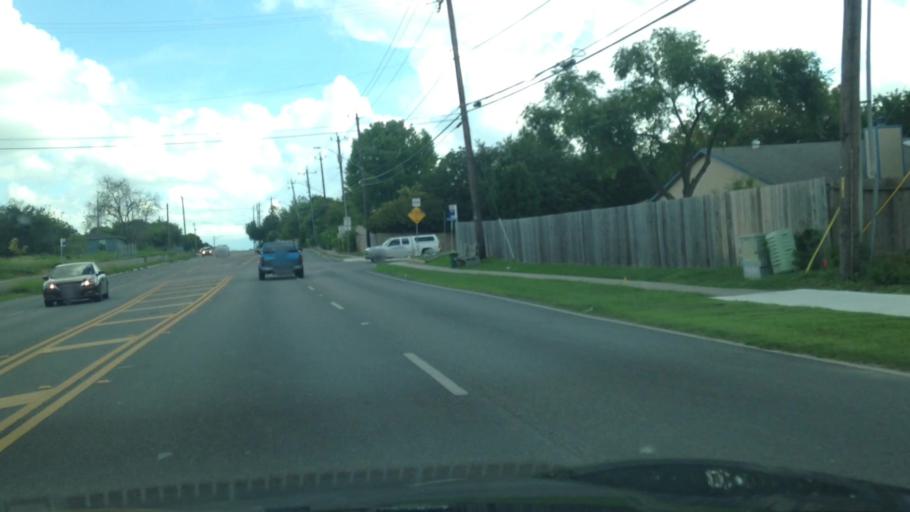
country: US
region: Texas
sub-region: Bexar County
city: Windcrest
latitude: 29.5732
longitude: -98.3978
